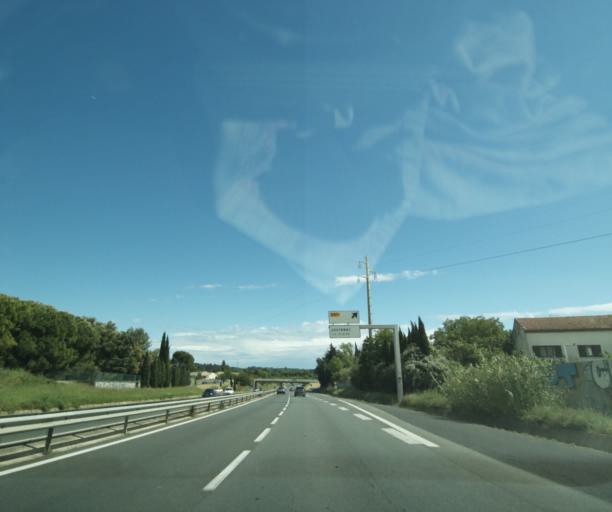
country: FR
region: Languedoc-Roussillon
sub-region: Departement de l'Herault
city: Juvignac
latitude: 43.6120
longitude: 3.8010
